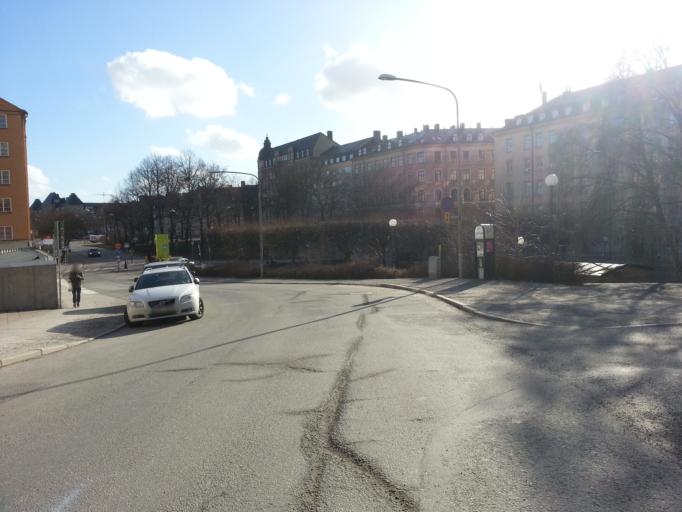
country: SE
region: Stockholm
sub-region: Stockholms Kommun
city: Stockholm
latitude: 59.3483
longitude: 18.0649
